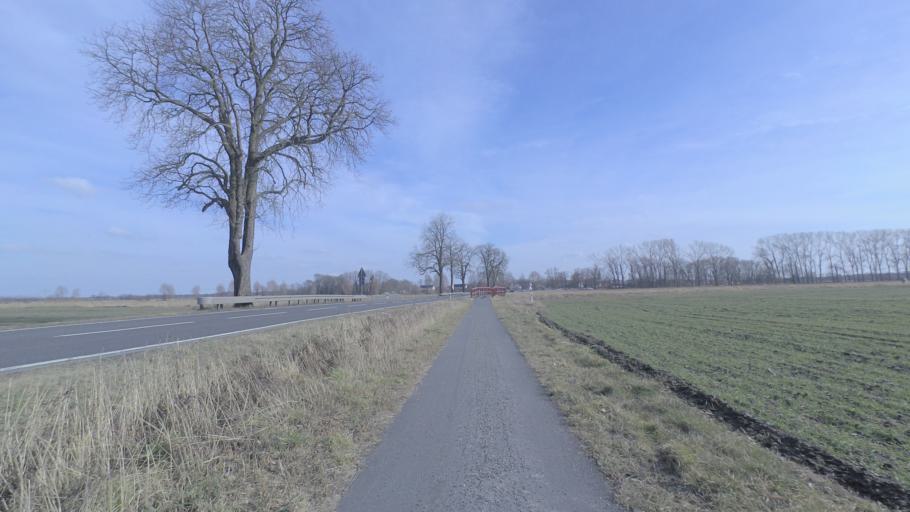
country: DE
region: Brandenburg
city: Ludwigsfelde
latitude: 52.2747
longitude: 13.3004
